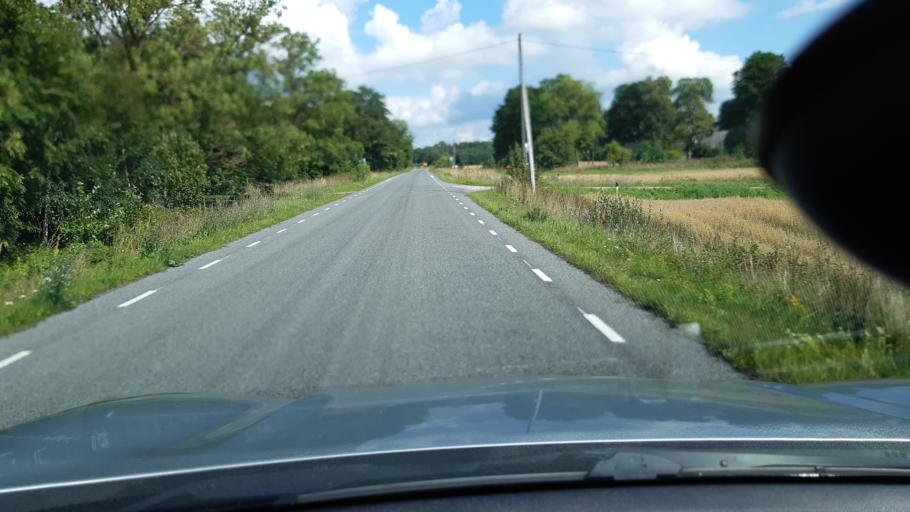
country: EE
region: Raplamaa
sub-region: Kehtna vald
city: Kehtna
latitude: 58.8755
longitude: 25.0097
